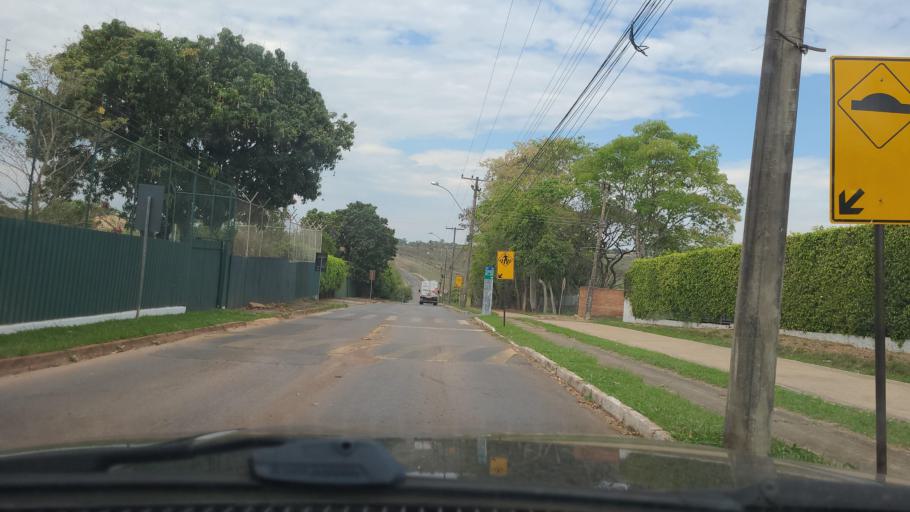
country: BR
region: Federal District
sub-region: Brasilia
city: Brasilia
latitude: -15.8597
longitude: -47.8585
